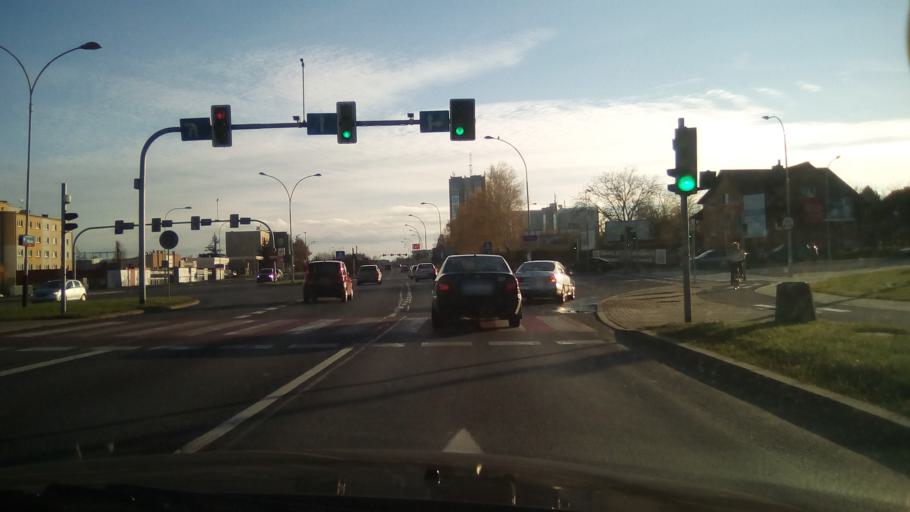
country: PL
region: Subcarpathian Voivodeship
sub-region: Rzeszow
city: Rzeszow
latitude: 50.0309
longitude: 21.9760
